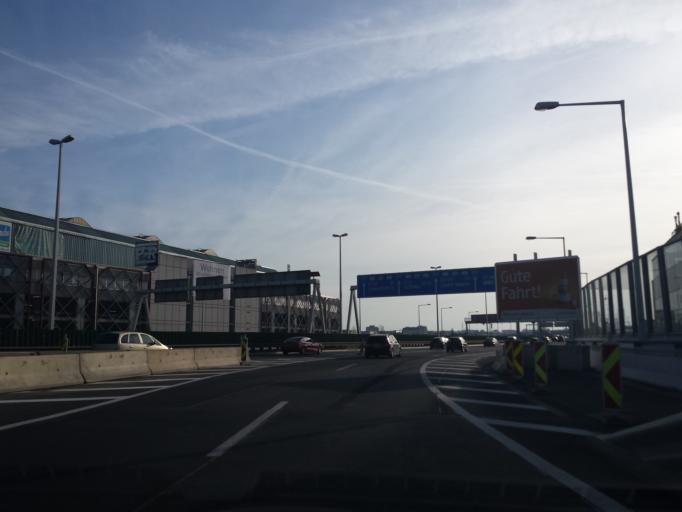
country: AT
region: Vienna
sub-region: Wien Stadt
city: Vienna
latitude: 48.1913
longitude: 16.4133
